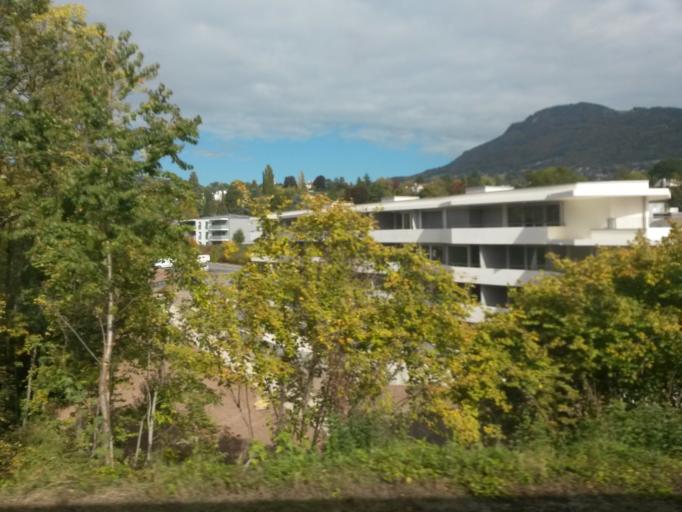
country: CH
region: Vaud
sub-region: Riviera-Pays-d'Enhaut District
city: La Tour-de-Peilz
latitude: 46.4492
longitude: 6.8713
